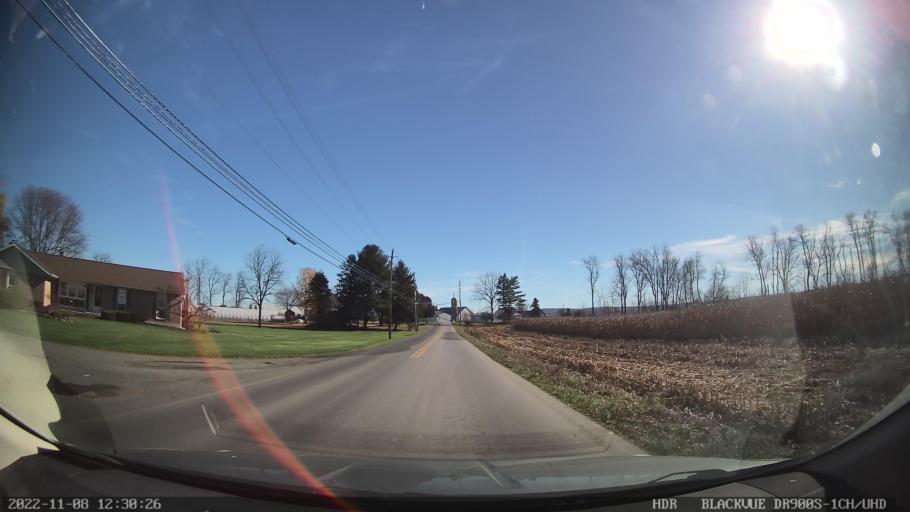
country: US
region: Pennsylvania
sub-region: Berks County
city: Kutztown
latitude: 40.5203
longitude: -75.7525
